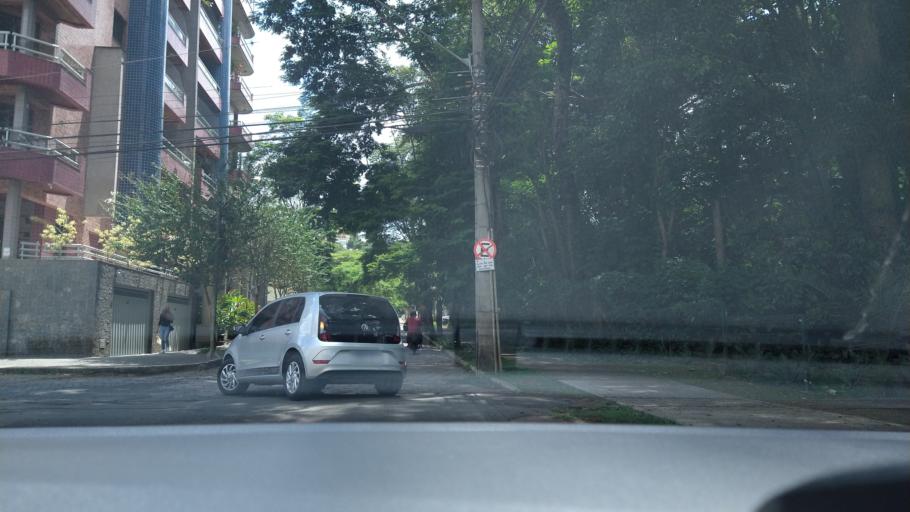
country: BR
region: Minas Gerais
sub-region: Vicosa
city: Vicosa
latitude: -20.7566
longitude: -42.8747
